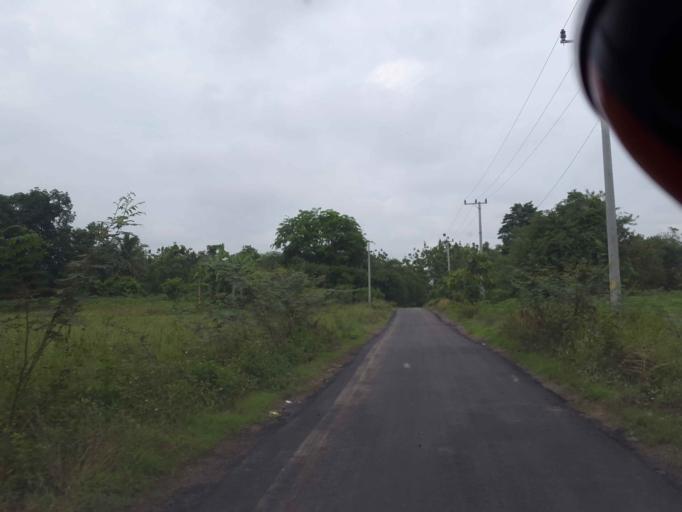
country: ID
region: Lampung
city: Natar
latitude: -5.2661
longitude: 105.2000
